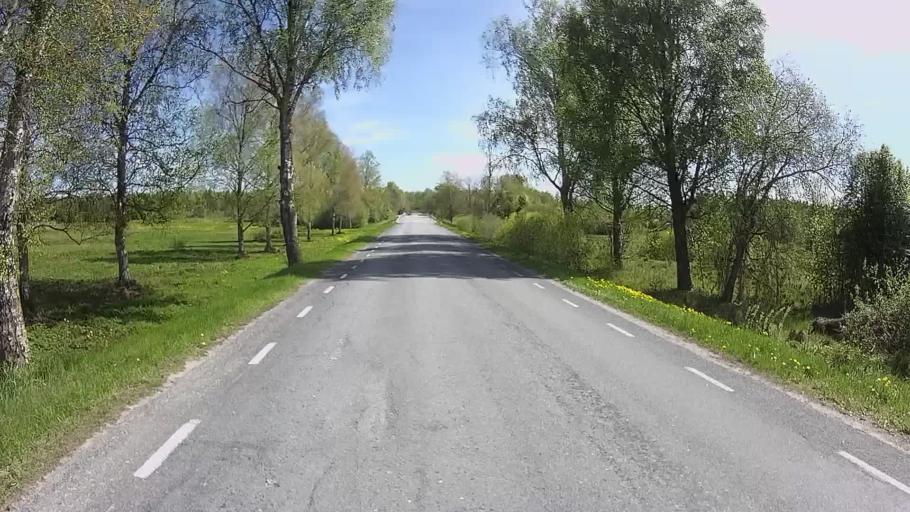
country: LV
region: Apes Novads
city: Ape
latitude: 57.6193
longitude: 26.6029
